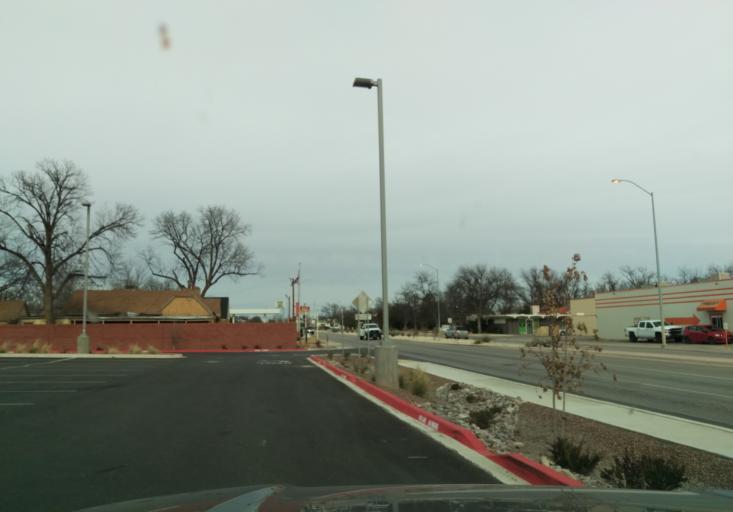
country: US
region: New Mexico
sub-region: Eddy County
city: Carlsbad
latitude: 32.4289
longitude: -104.2291
